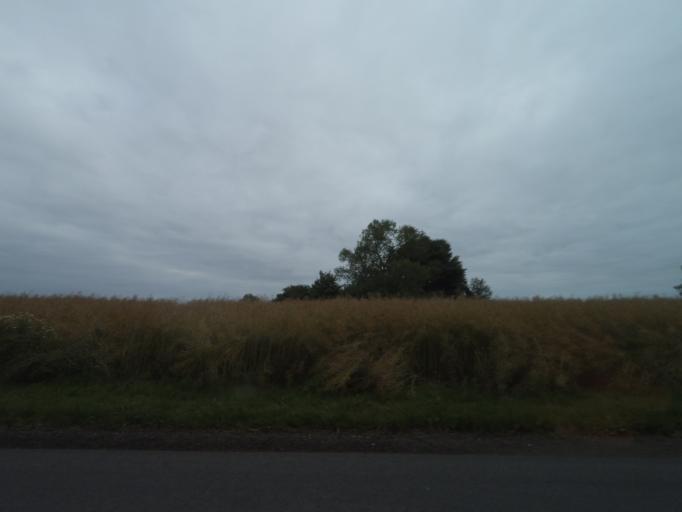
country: DK
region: South Denmark
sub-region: Nordfyns Kommune
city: Otterup
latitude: 55.5517
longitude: 10.4365
